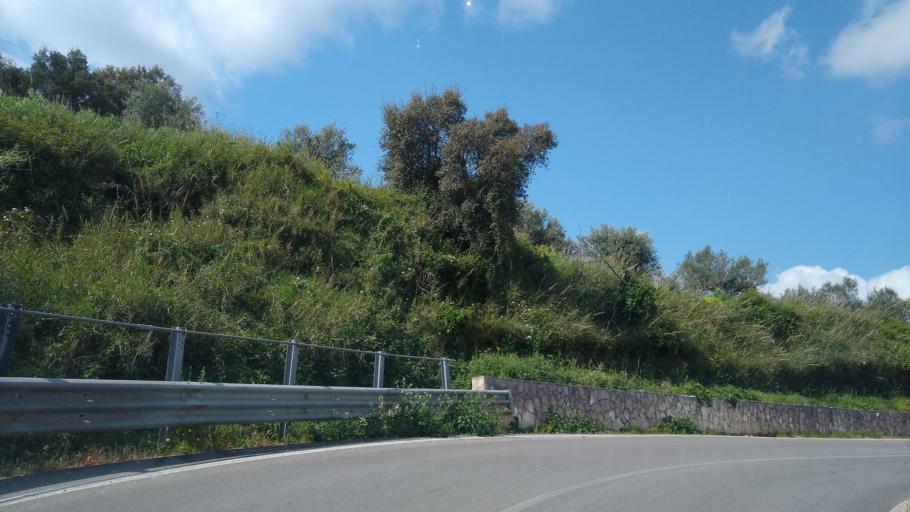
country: IT
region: Sicily
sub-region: Trapani
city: Calatafimi
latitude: 37.9568
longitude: 12.8691
